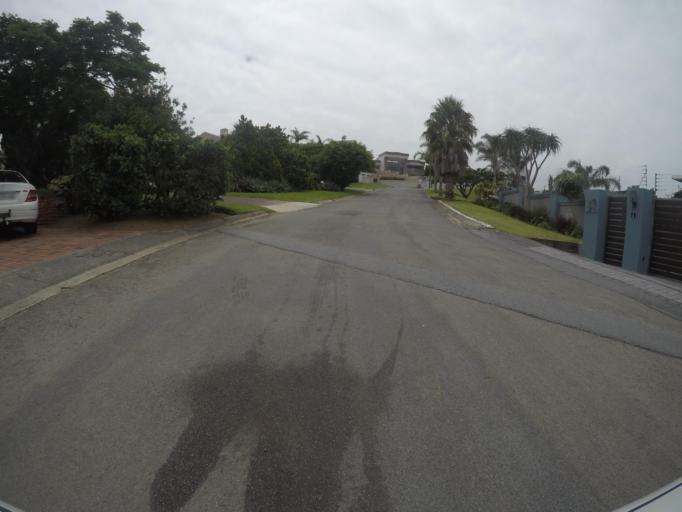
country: ZA
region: Eastern Cape
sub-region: Buffalo City Metropolitan Municipality
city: East London
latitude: -32.9792
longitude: 27.9438
